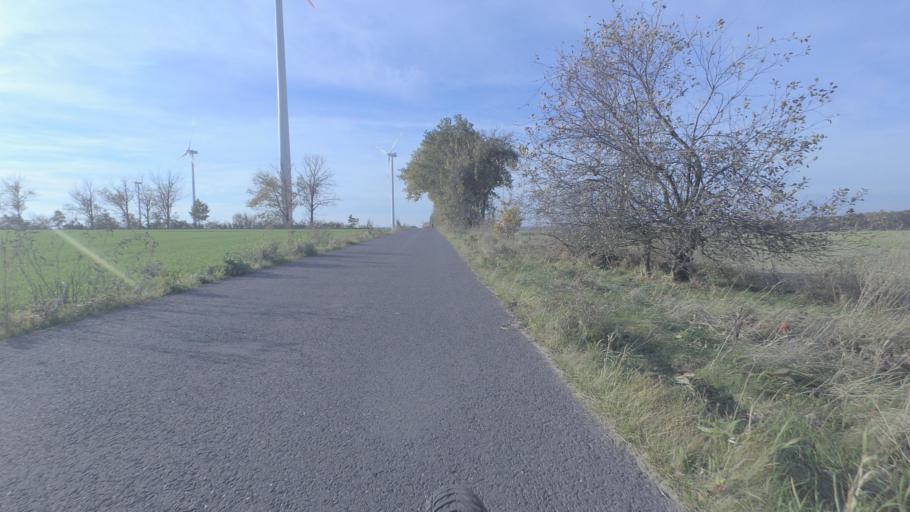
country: DE
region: Brandenburg
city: Trebbin
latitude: 52.2079
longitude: 13.3023
